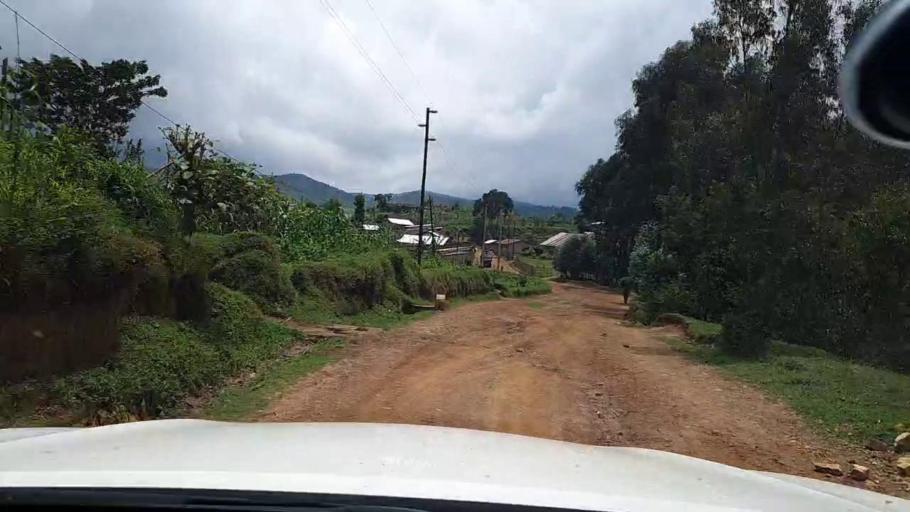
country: RW
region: Western Province
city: Kibuye
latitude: -2.1690
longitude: 29.4289
